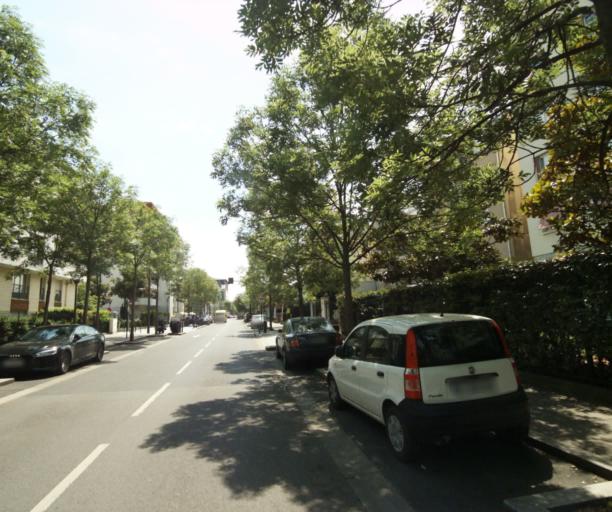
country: FR
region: Ile-de-France
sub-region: Departement des Hauts-de-Seine
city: Colombes
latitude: 48.9090
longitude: 2.2576
